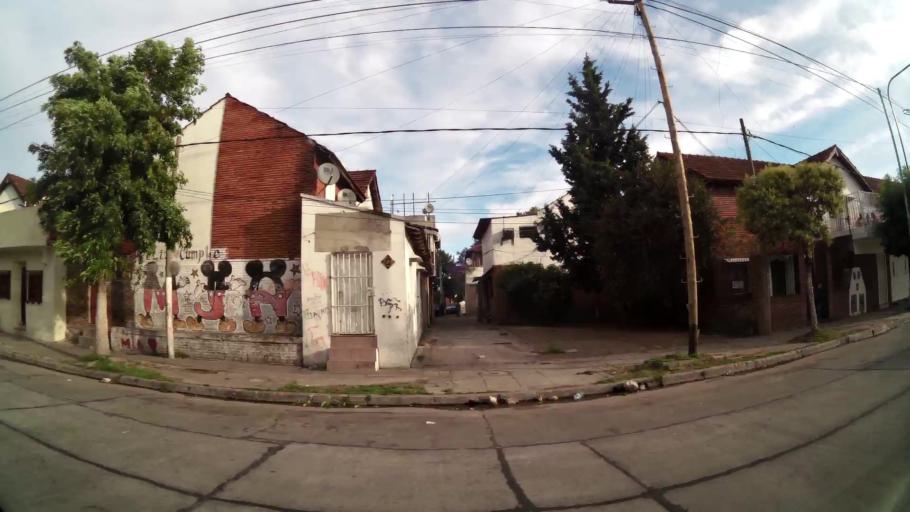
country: AR
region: Buenos Aires F.D.
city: Villa Lugano
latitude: -34.6465
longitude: -58.4354
